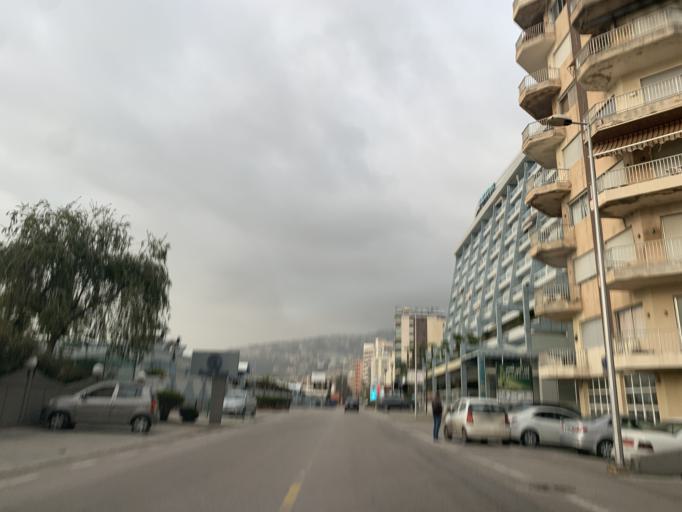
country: LB
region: Mont-Liban
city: Djounie
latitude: 33.9992
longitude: 35.6440
